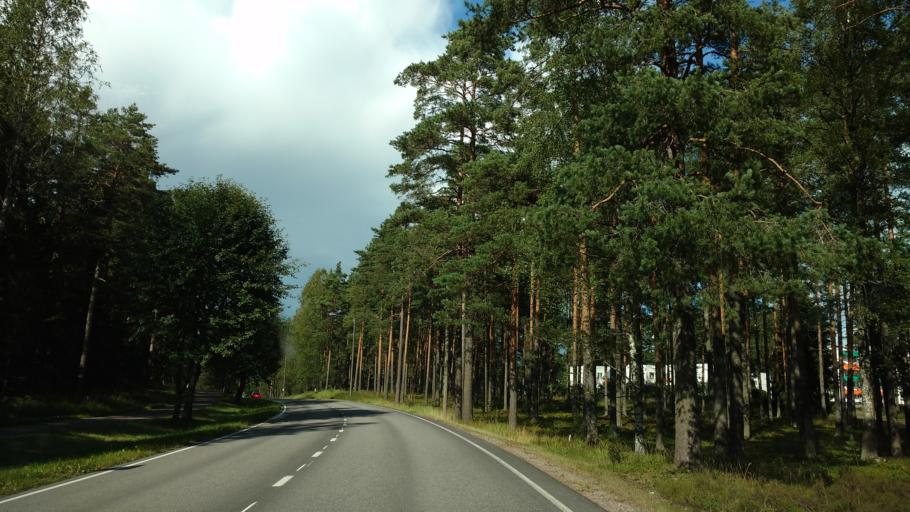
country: FI
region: Varsinais-Suomi
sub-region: Turku
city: Paimio
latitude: 60.4634
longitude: 22.7319
